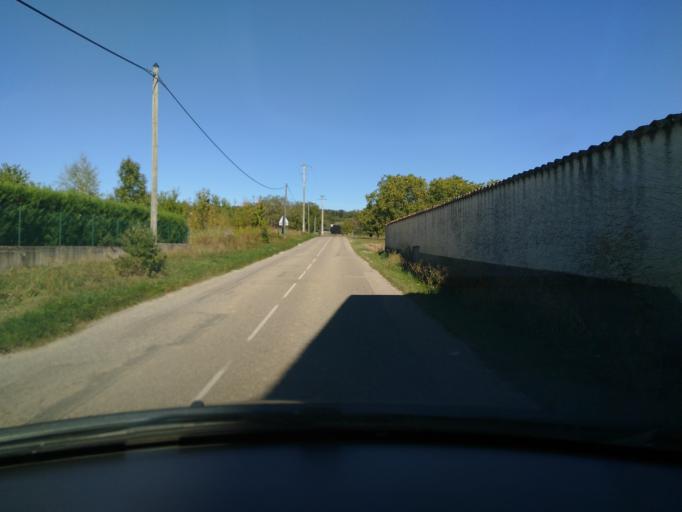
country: FR
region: Rhone-Alpes
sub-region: Departement de l'Isere
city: La Murette
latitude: 45.3733
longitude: 5.5244
